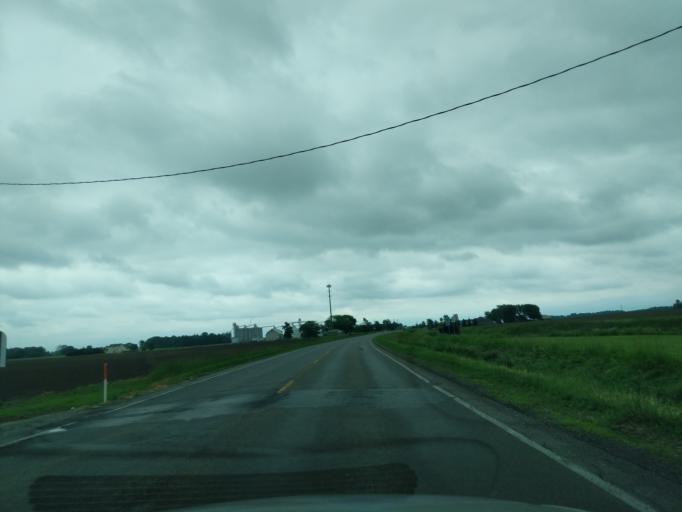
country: US
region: Indiana
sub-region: Tipton County
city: Tipton
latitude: 40.2835
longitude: -86.0192
